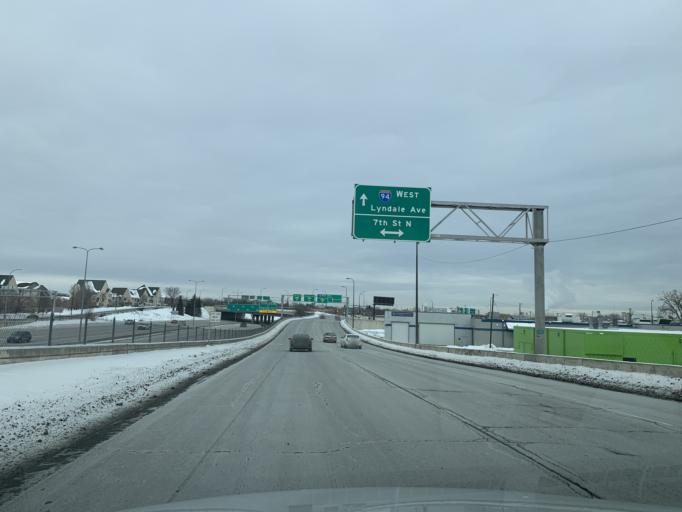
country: US
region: Minnesota
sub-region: Hennepin County
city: Minneapolis
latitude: 44.9849
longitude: -93.2877
